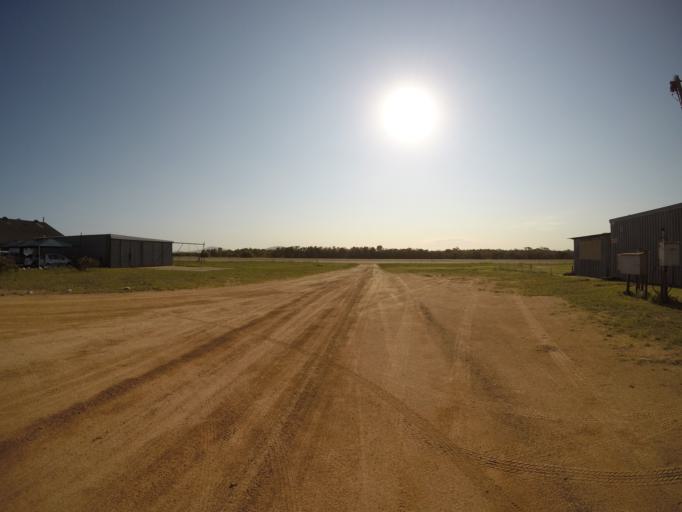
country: ZA
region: Western Cape
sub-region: City of Cape Town
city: Kraaifontein
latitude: -33.7704
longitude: 18.7421
